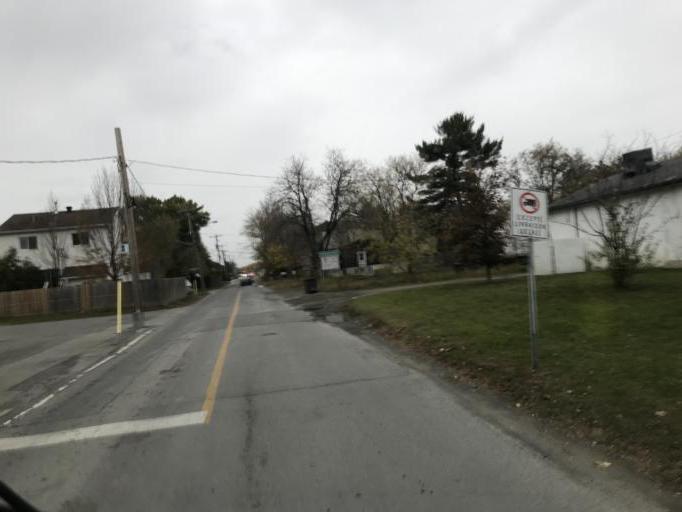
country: CA
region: Quebec
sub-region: Lanaudiere
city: Lorraine
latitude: 45.6841
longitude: -73.7888
